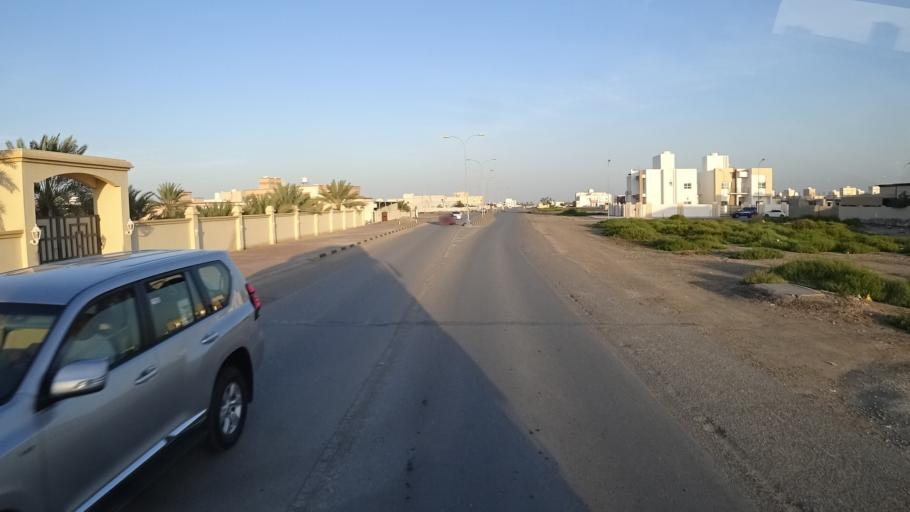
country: OM
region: Al Batinah
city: Barka'
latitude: 23.7020
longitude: 57.9288
